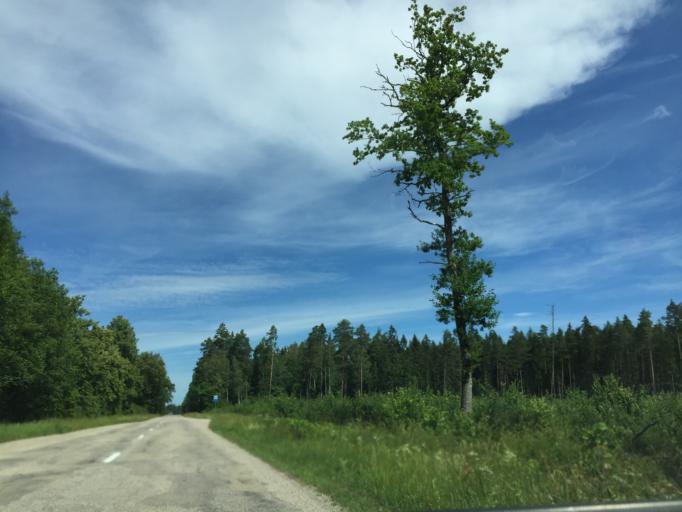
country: LV
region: Dundaga
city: Dundaga
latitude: 57.5712
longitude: 22.3065
